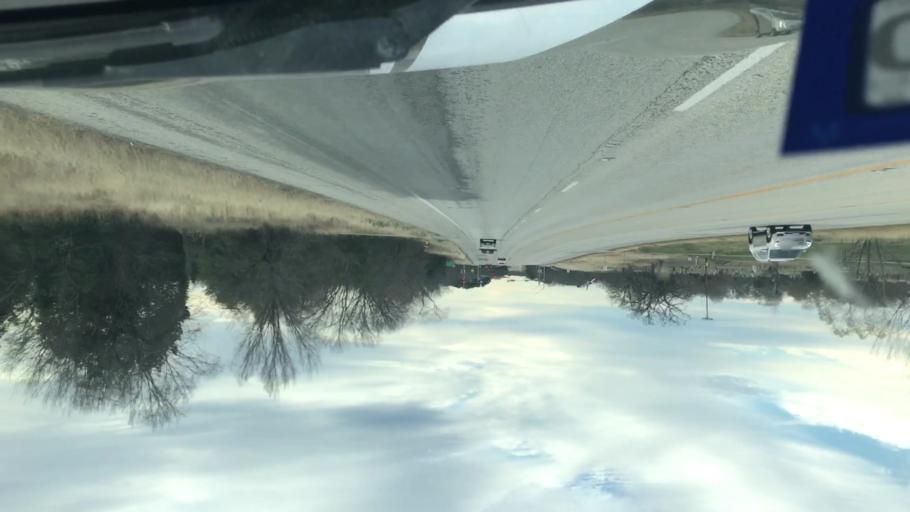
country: US
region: Texas
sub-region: Bastrop County
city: Camp Swift
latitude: 30.2822
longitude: -97.2443
